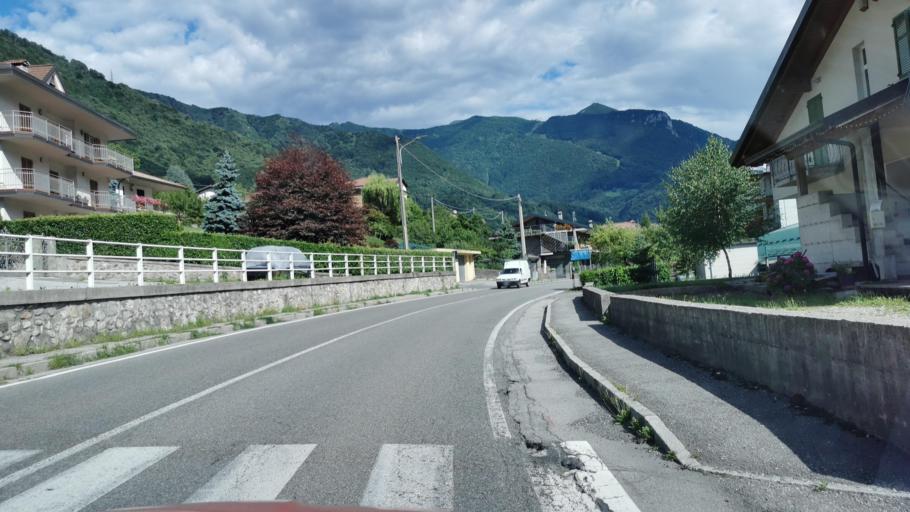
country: IT
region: Lombardy
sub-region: Provincia di Lecco
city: Primaluna
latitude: 45.9849
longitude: 9.4344
